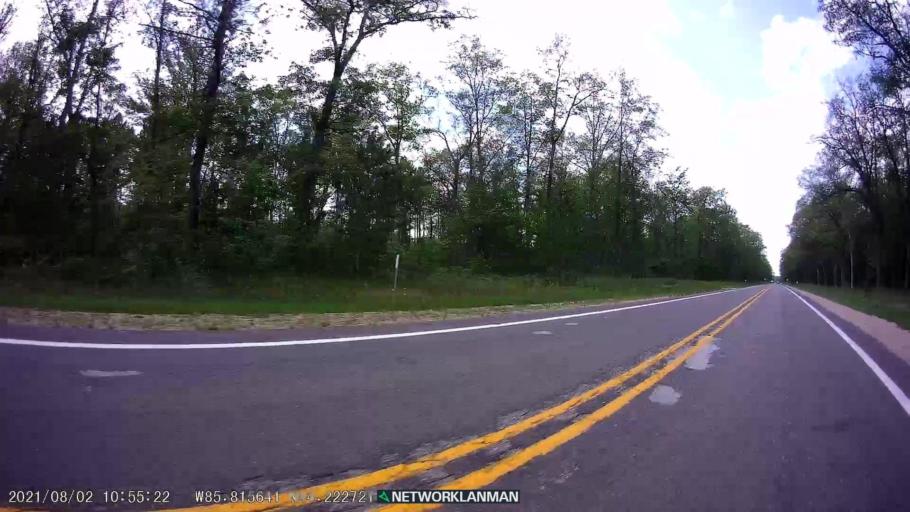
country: US
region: Michigan
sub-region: Lake County
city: Baldwin
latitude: 44.2228
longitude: -85.8161
